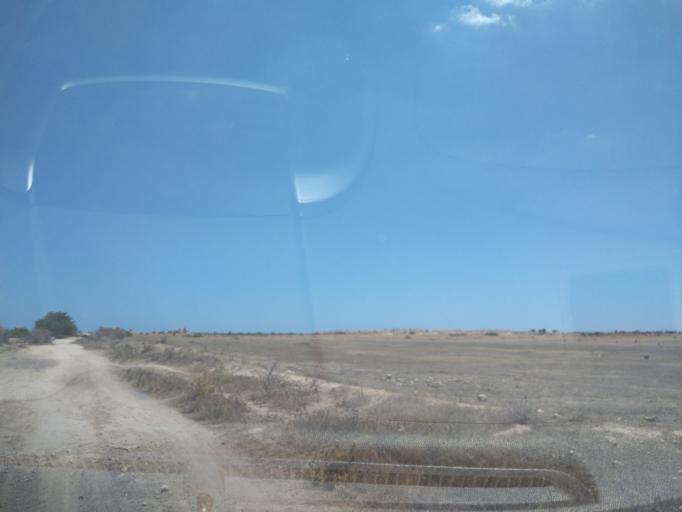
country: TN
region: Susah
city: Harqalah
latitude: 36.1717
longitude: 10.4405
